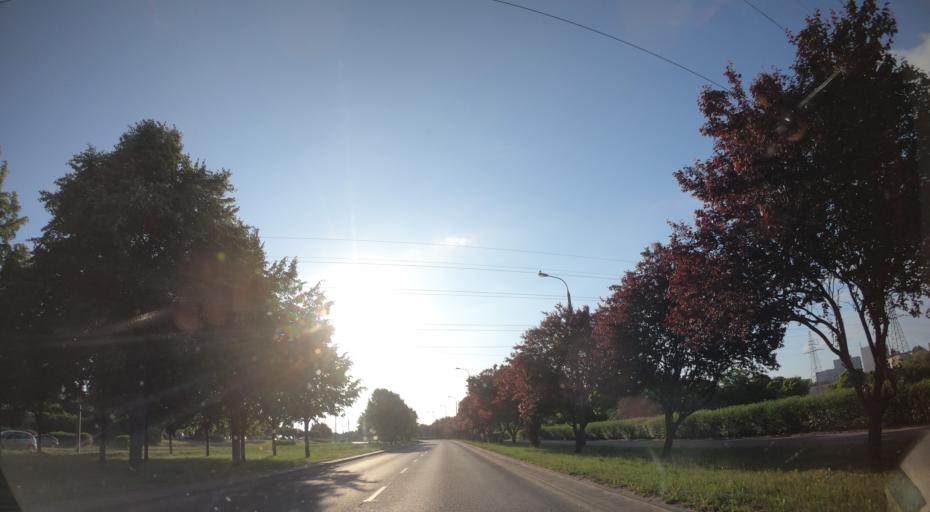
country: PL
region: Lubusz
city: Gorzow Wielkopolski
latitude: 52.7576
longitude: 15.2663
